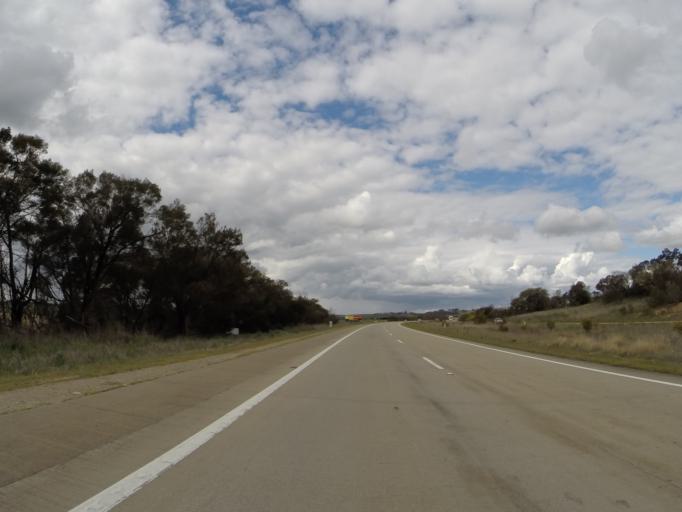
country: AU
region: New South Wales
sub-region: Yass Valley
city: Gundaroo
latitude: -34.8150
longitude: 149.4175
